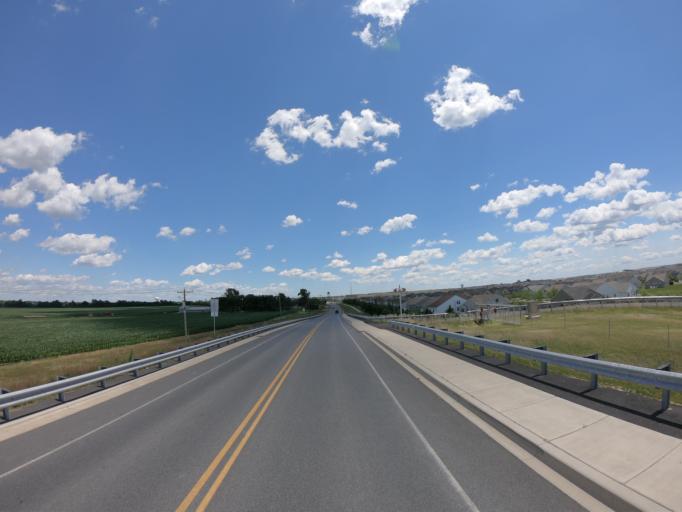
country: US
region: Delaware
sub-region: New Castle County
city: Middletown
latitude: 39.4560
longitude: -75.7408
